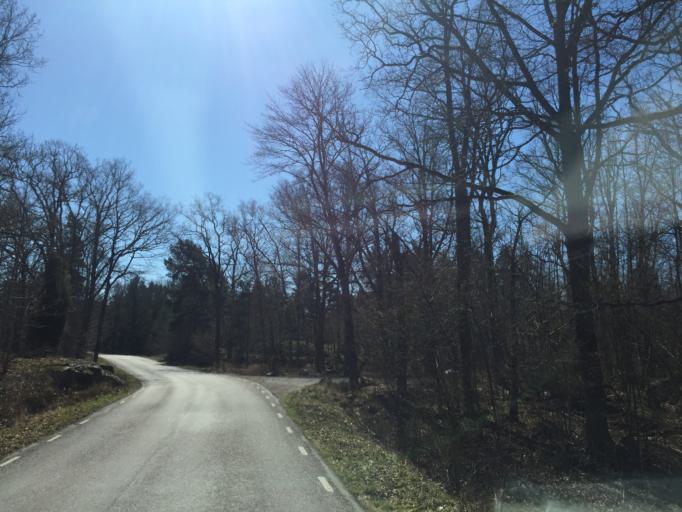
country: SE
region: Kalmar
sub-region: Oskarshamns Kommun
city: Oskarshamn
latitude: 57.2386
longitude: 16.4775
